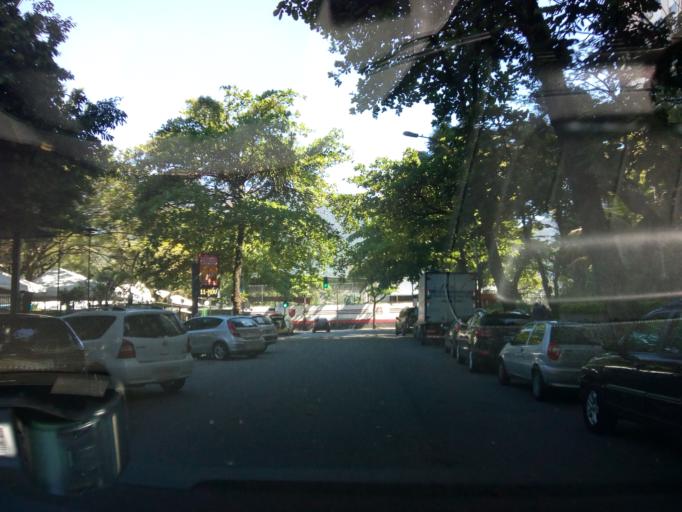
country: BR
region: Rio de Janeiro
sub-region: Rio De Janeiro
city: Rio de Janeiro
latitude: -22.9805
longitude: -43.2210
